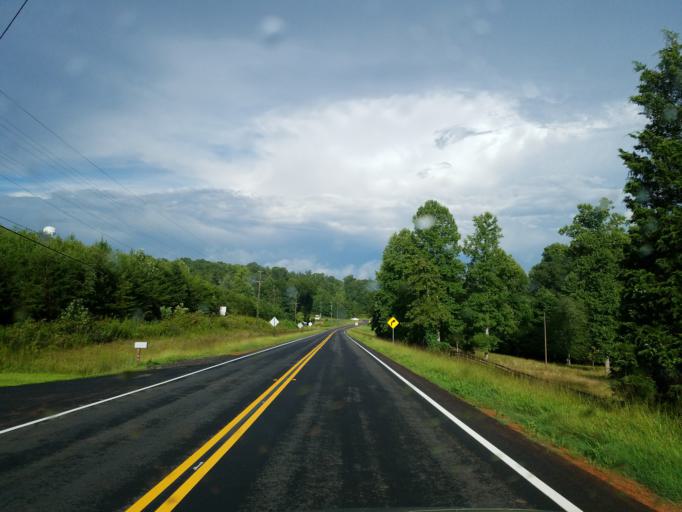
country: US
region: Georgia
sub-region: White County
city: Cleveland
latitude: 34.6130
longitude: -83.7836
